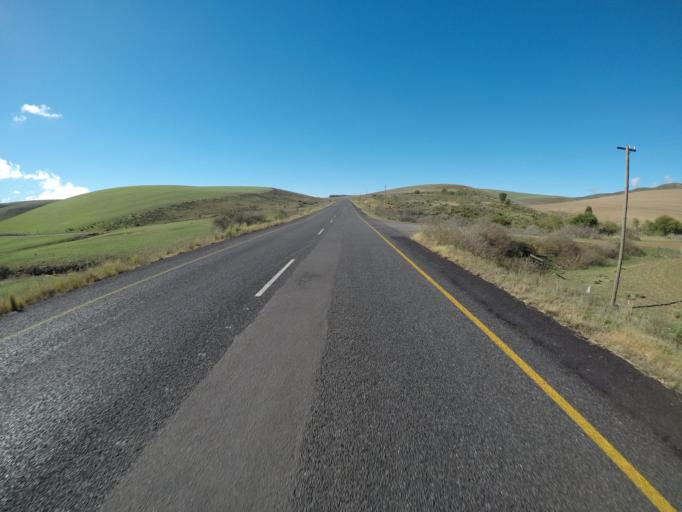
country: ZA
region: Western Cape
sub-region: Overberg District Municipality
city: Caledon
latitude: -34.1485
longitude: 19.4852
